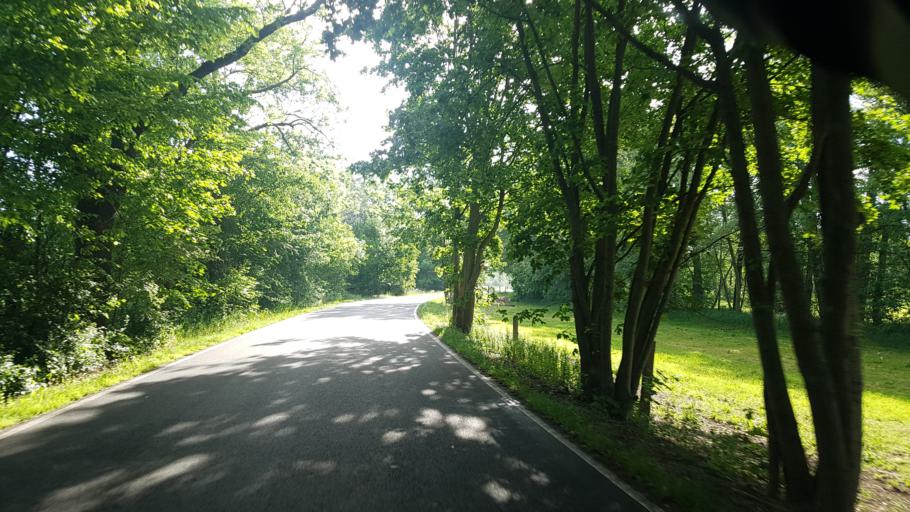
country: DE
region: Brandenburg
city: Luckau
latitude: 51.8269
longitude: 13.7352
